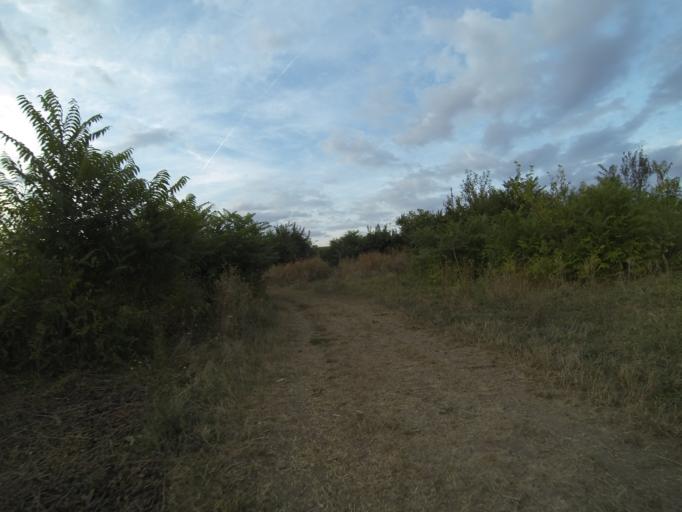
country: RO
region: Dolj
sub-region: Comuna Ceratu
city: Ceratu
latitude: 44.0916
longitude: 23.6694
